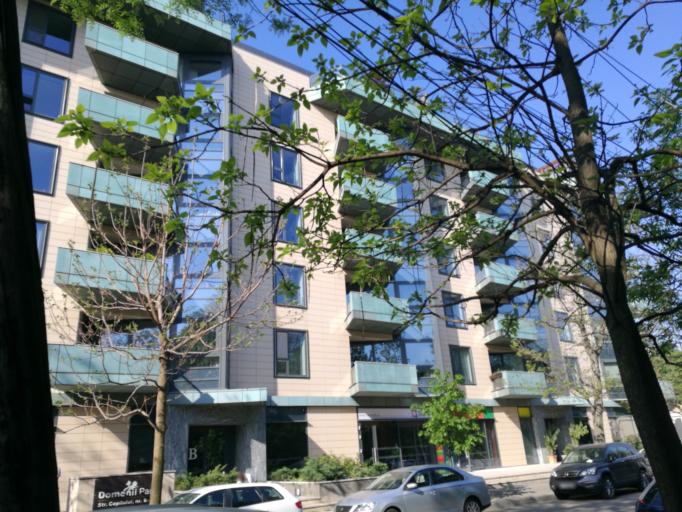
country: RO
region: Ilfov
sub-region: Comuna Chiajna
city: Rosu
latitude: 44.4651
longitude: 26.0606
